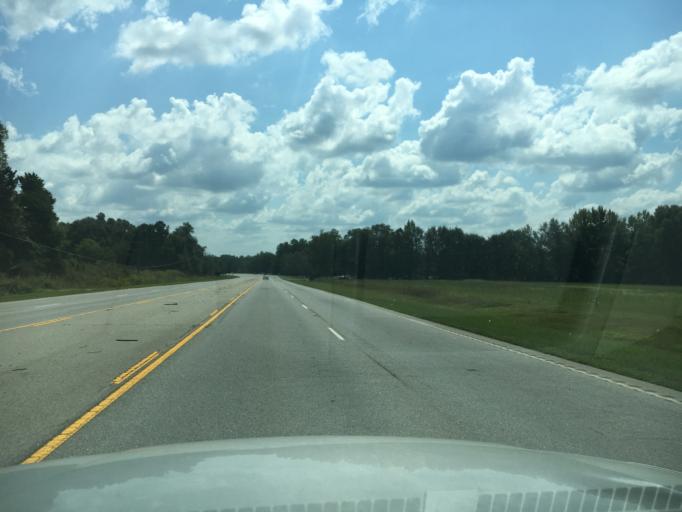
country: US
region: South Carolina
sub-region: Anderson County
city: Honea Path
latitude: 34.5708
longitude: -82.3330
